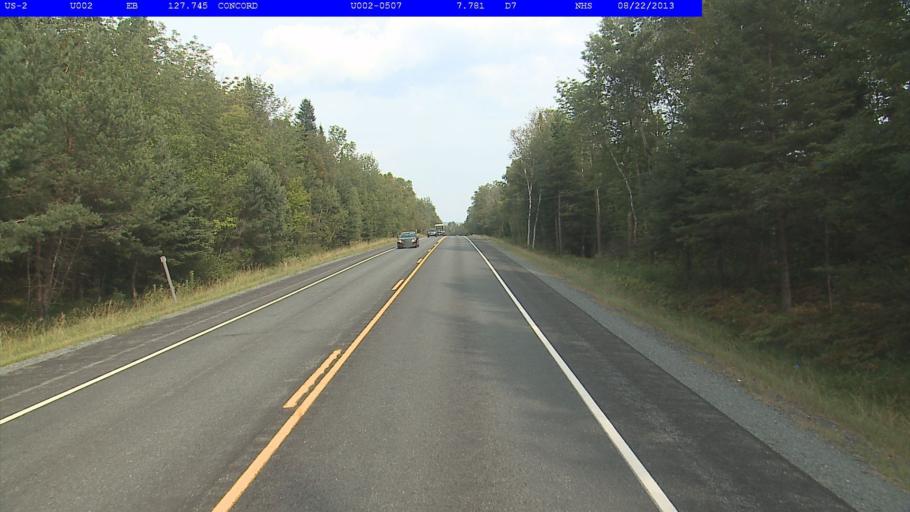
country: US
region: New Hampshire
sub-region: Grafton County
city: Littleton
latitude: 44.4523
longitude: -71.8206
